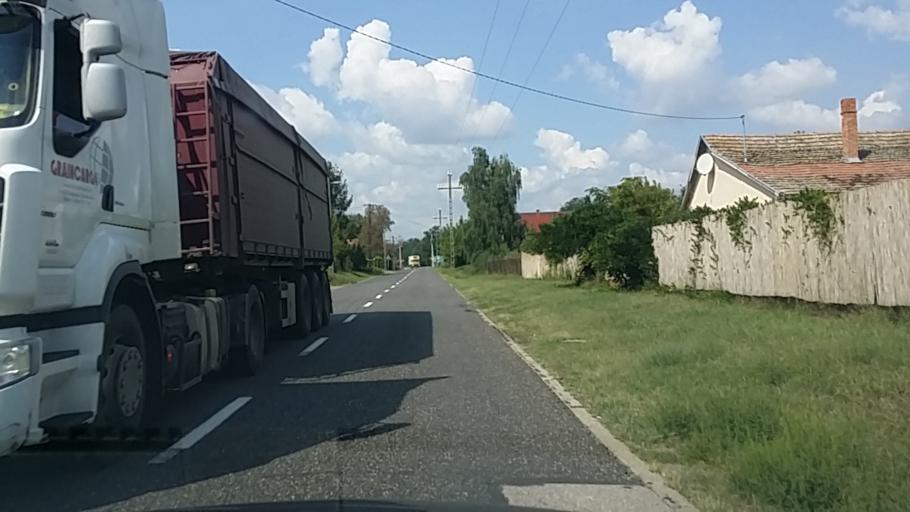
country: HU
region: Bacs-Kiskun
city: Lakitelek
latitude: 46.8661
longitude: 19.9620
